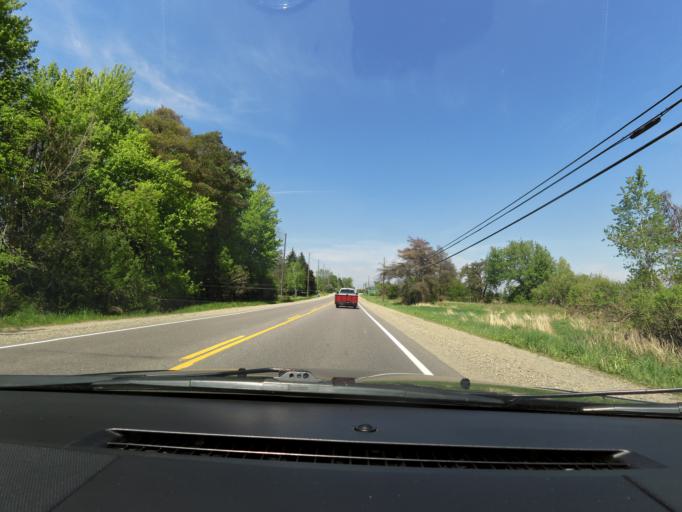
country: CA
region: Ontario
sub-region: Wellington County
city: Guelph
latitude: 43.5977
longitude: -80.1710
